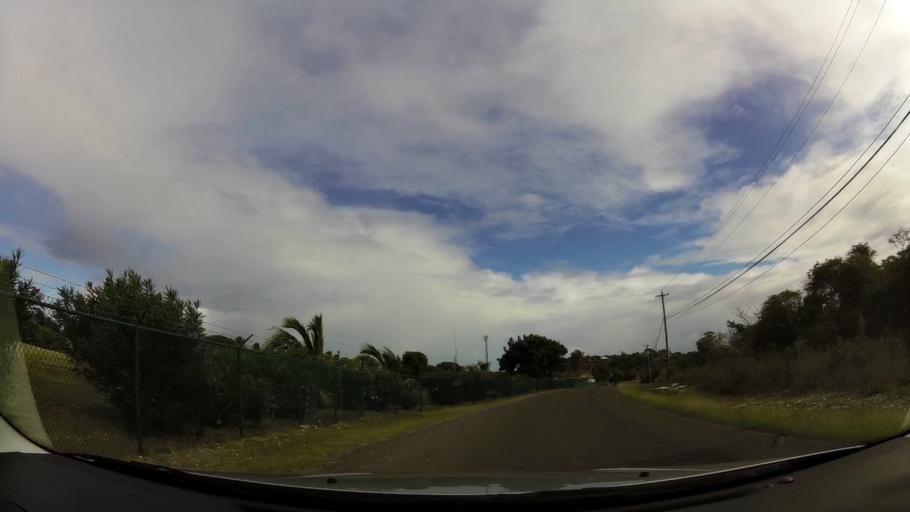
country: AG
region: Saint Peter
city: Parham
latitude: 17.0949
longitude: -61.6911
